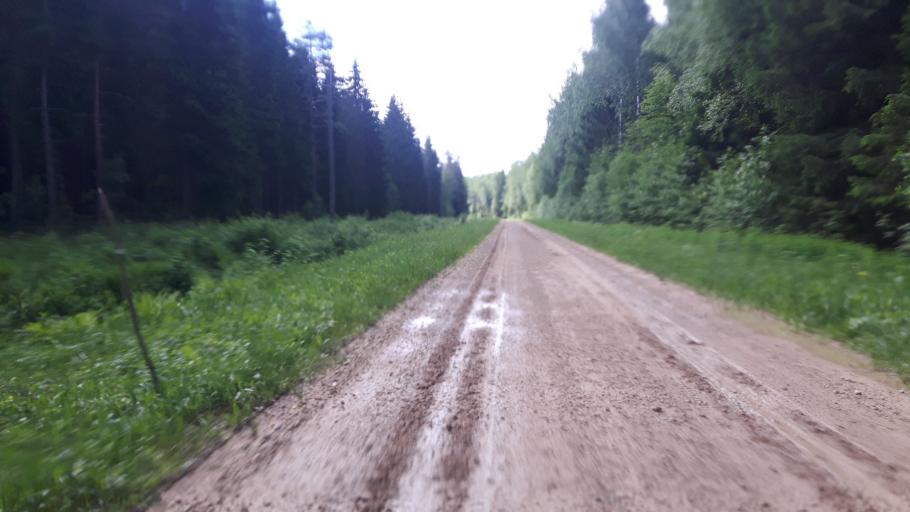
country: EE
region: Paernumaa
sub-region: Vaendra vald (alev)
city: Vandra
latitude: 58.7148
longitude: 25.0425
